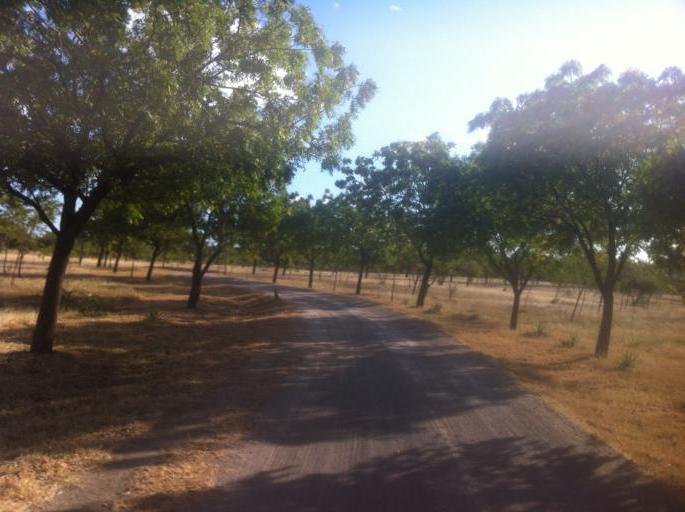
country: NI
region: Managua
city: Carlos Fonseca Amador
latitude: 11.9164
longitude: -86.5965
